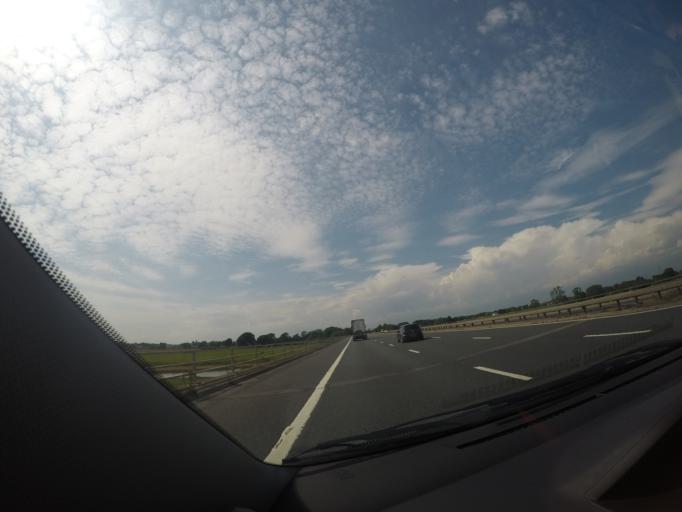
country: GB
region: England
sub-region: Cumbria
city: Scotby
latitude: 54.9085
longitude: -2.8939
